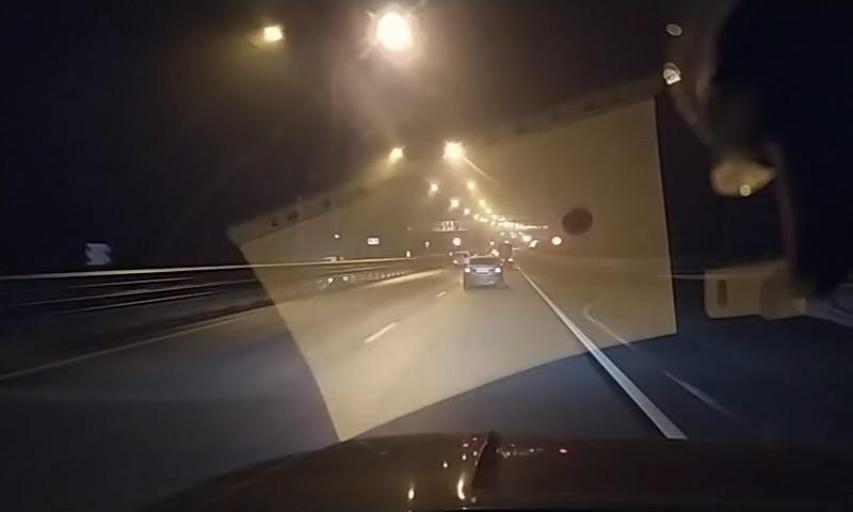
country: RU
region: Leningrad
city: Bugry
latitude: 60.1236
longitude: 30.3847
